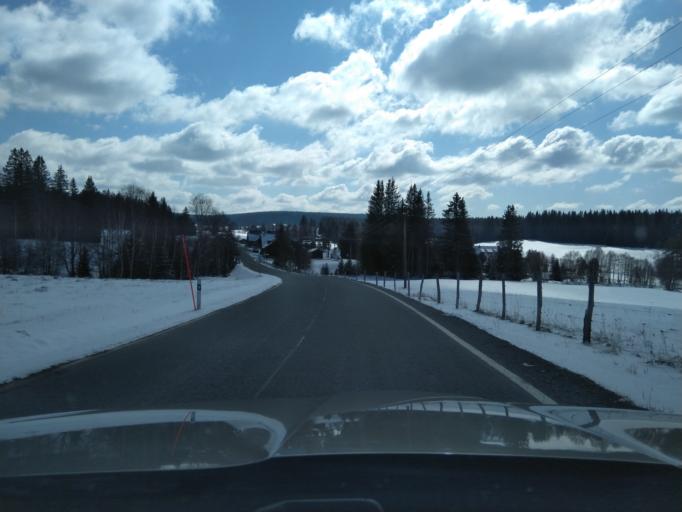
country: CZ
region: Plzensky
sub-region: Okres Klatovy
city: Kasperske Hory
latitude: 49.0558
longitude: 13.5610
